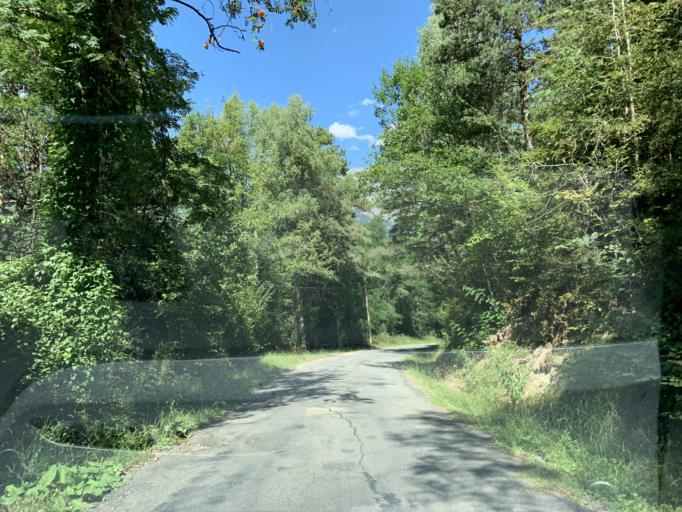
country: ES
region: Aragon
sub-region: Provincia de Huesca
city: Hoz de Jaca
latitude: 42.6978
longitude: -0.3057
